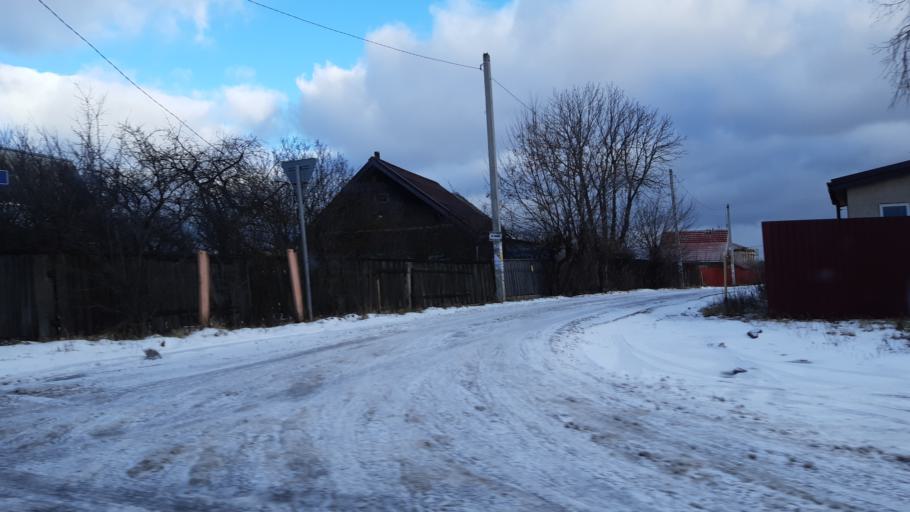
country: RU
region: Moskovskaya
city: Noginsk-9
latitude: 55.9871
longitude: 38.5426
